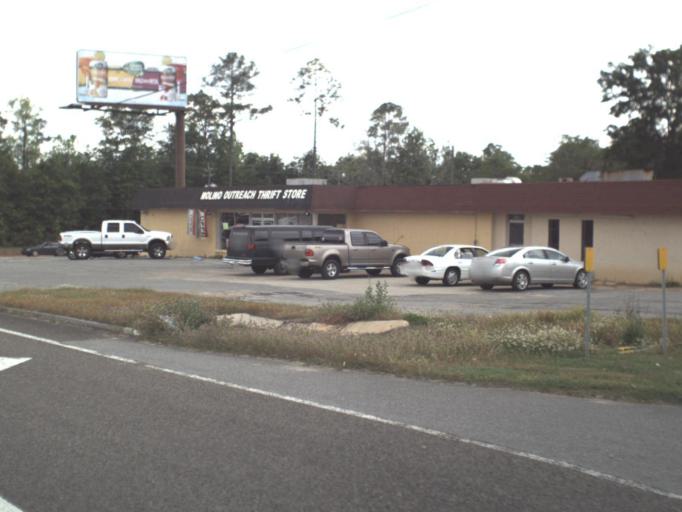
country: US
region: Florida
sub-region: Escambia County
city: Molino
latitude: 30.7178
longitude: -87.3499
